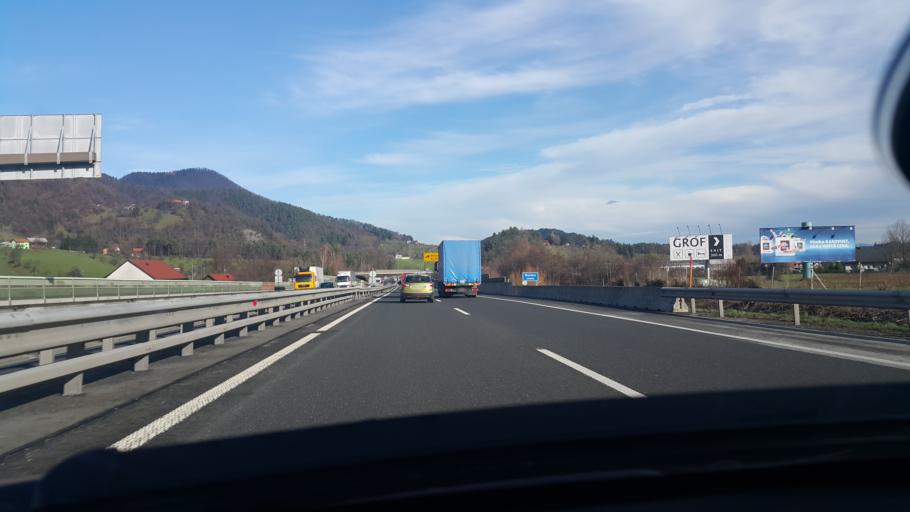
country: SI
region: Vransko
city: Vransko
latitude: 46.2475
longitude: 14.9678
